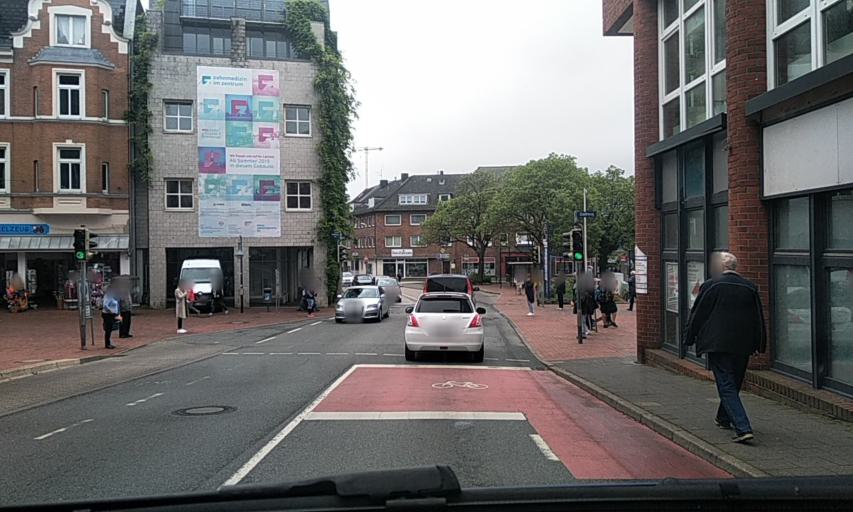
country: DE
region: Schleswig-Holstein
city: Schleswig
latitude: 54.5170
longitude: 9.5652
